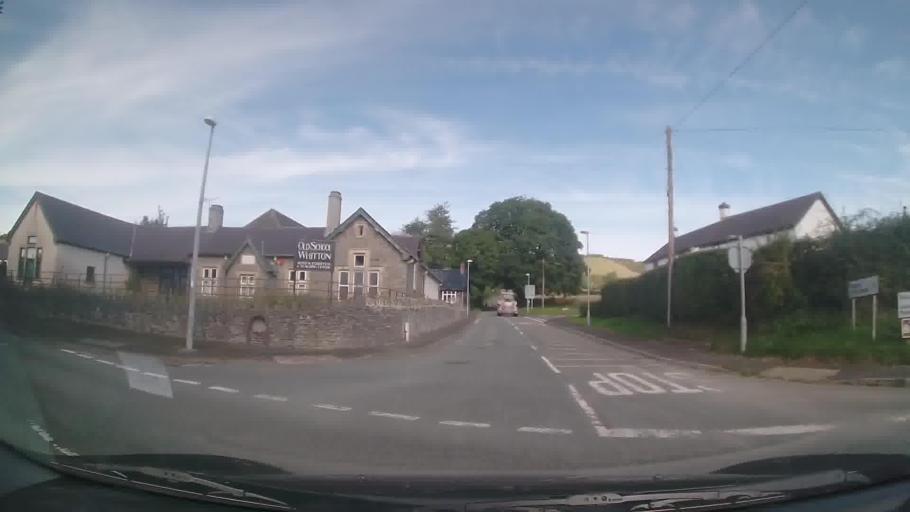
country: GB
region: Wales
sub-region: Sir Powys
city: Whitton
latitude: 52.2985
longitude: -3.0688
